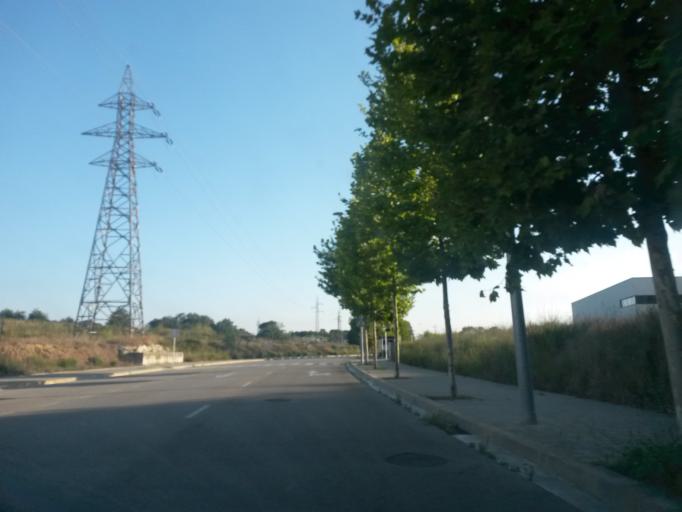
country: ES
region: Catalonia
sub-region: Provincia de Girona
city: Fornells de la Selva
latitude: 41.9479
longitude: 2.8010
